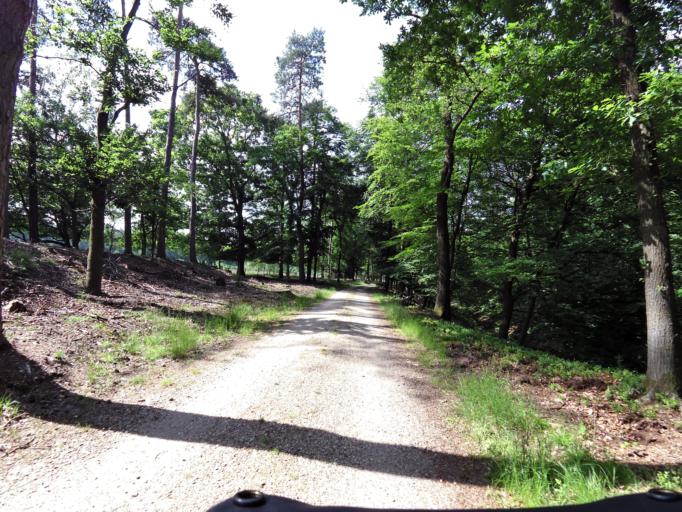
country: NL
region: Gelderland
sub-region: Gemeente Apeldoorn
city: Loenen
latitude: 52.1138
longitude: 5.9857
